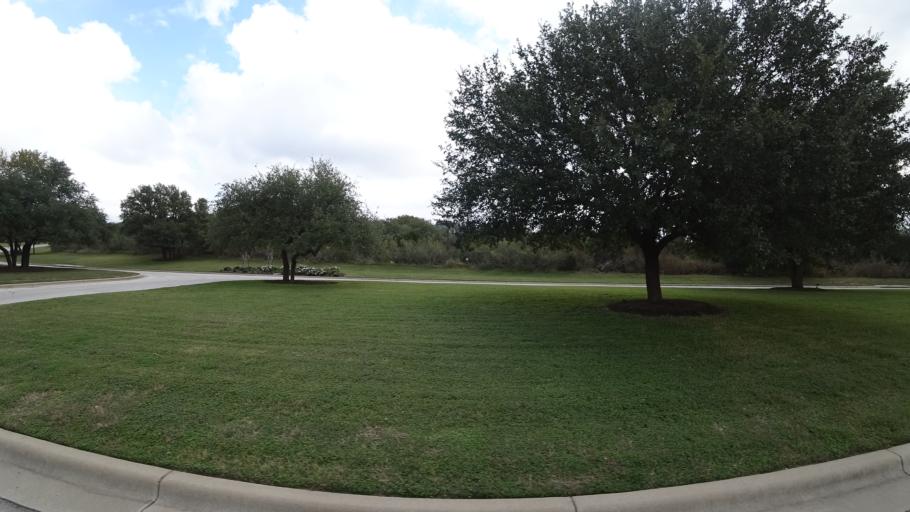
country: US
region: Texas
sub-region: Travis County
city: Bee Cave
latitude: 30.3097
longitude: -97.9044
